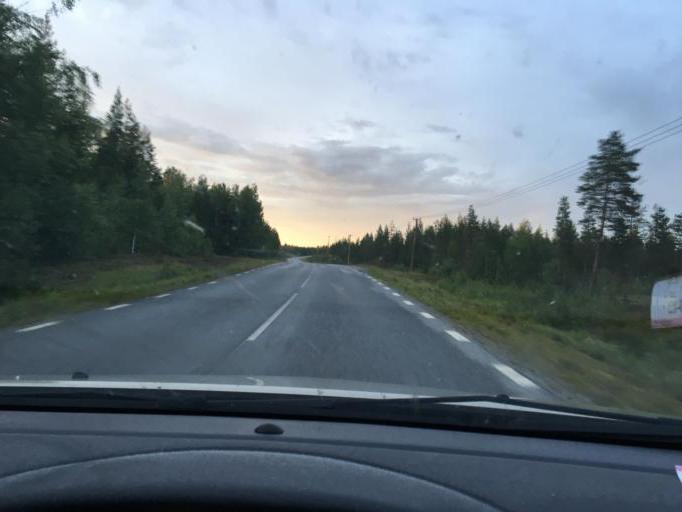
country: SE
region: Norrbotten
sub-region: Kalix Kommun
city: Toere
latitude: 66.0560
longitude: 22.5942
